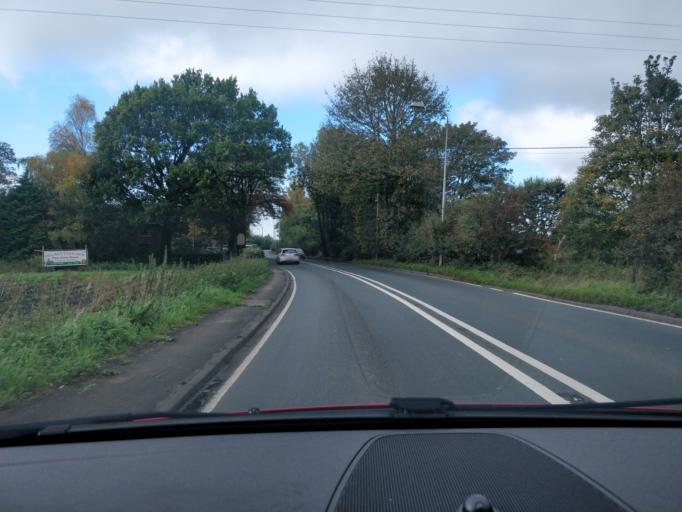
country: GB
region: England
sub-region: Lancashire
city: Ormskirk
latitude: 53.5882
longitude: -2.9147
